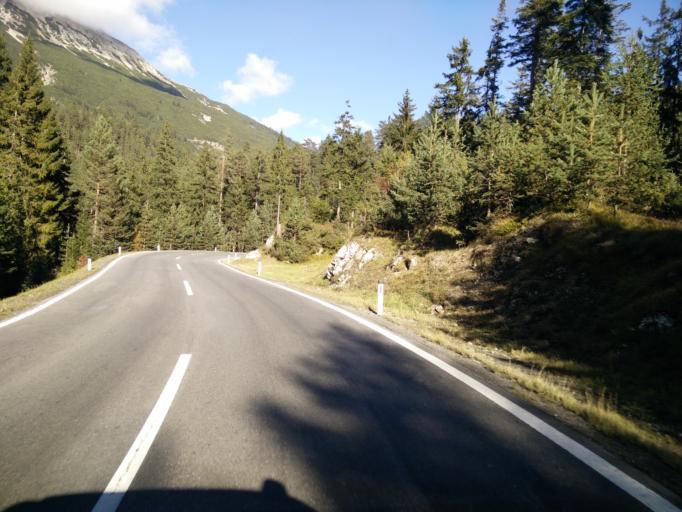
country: AT
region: Tyrol
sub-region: Politischer Bezirk Imst
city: Nassereith
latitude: 47.3599
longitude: 10.8294
